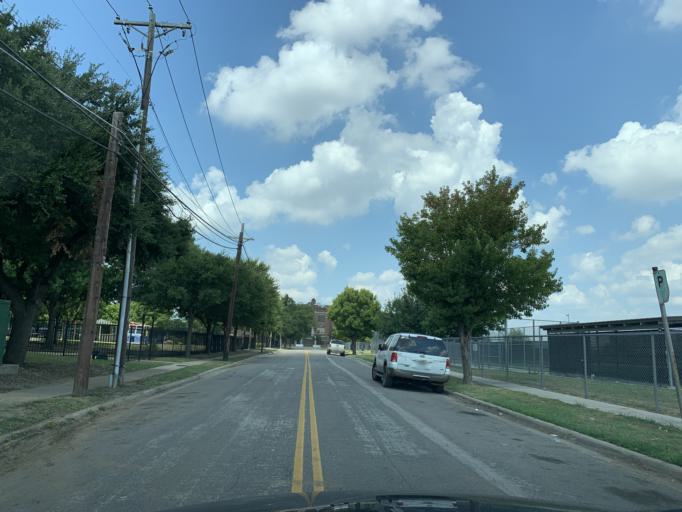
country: US
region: Texas
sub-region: Dallas County
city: Dallas
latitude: 32.7455
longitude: -96.8210
